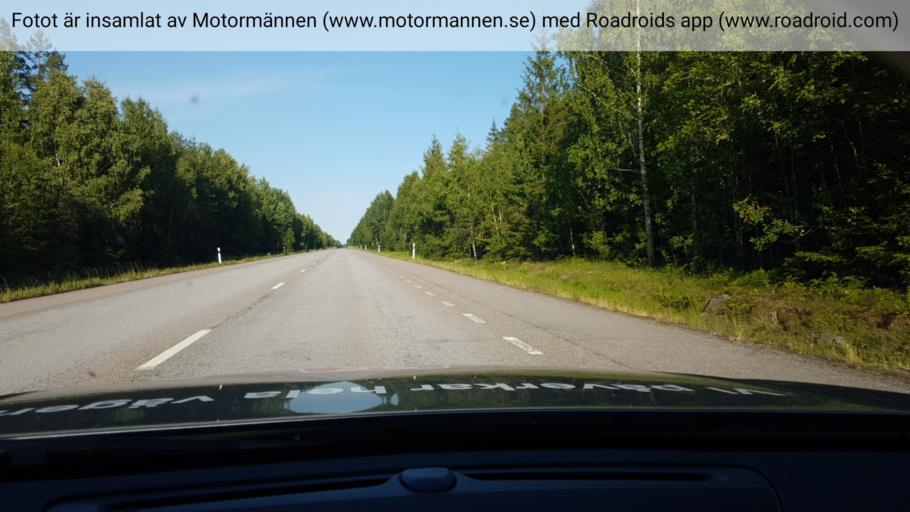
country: SE
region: Uppsala
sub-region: Osthammars Kommun
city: Gimo
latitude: 60.1640
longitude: 18.0979
